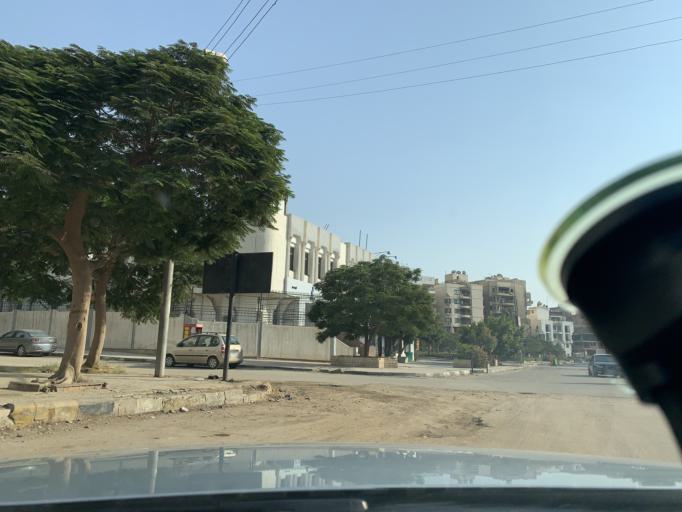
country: EG
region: Muhafazat al Qalyubiyah
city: Al Khankah
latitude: 30.1007
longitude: 31.3762
